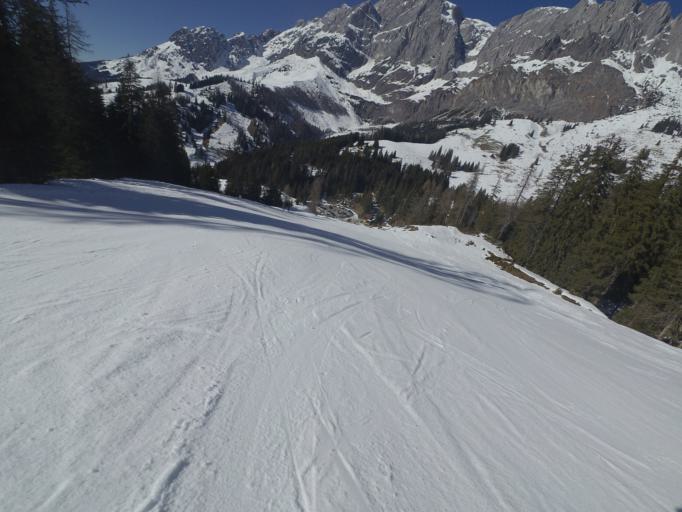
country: AT
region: Salzburg
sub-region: Politischer Bezirk Sankt Johann im Pongau
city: Muhlbach am Hochkonig
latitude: 47.3981
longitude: 13.1195
